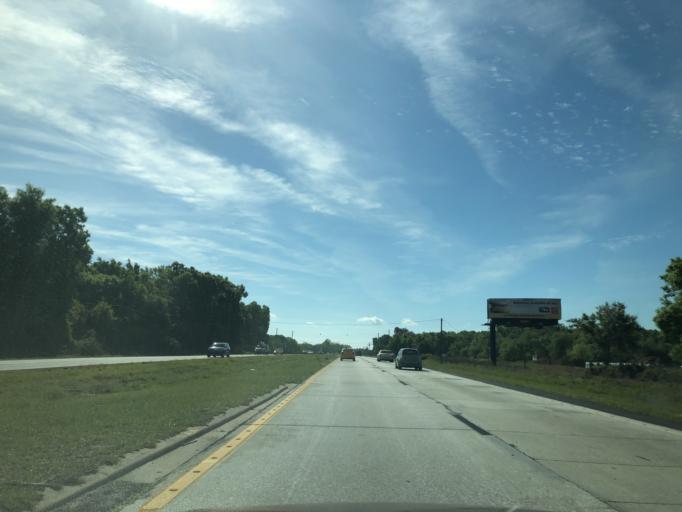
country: US
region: Florida
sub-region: Orange County
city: Zellwood
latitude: 28.7186
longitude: -81.5917
